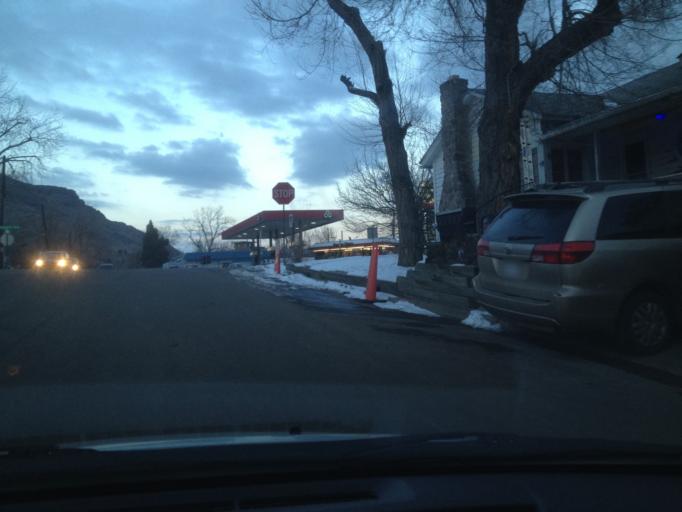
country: US
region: Colorado
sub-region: Jefferson County
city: Golden
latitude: 39.7606
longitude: -105.2267
